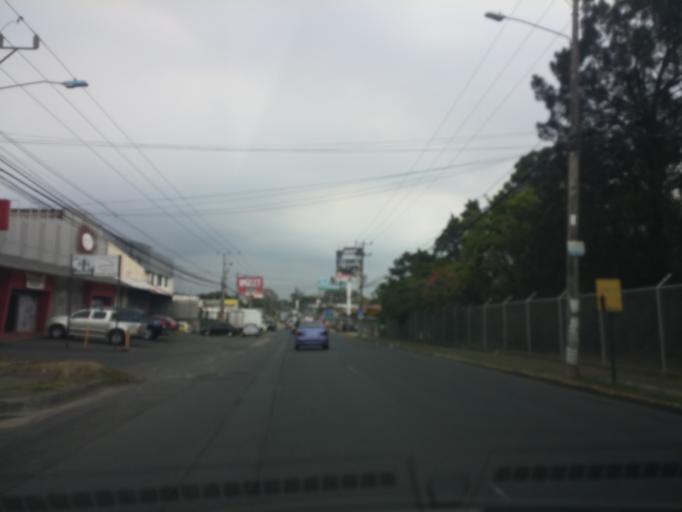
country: CR
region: Heredia
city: Llorente
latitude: 9.9810
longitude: -84.1509
